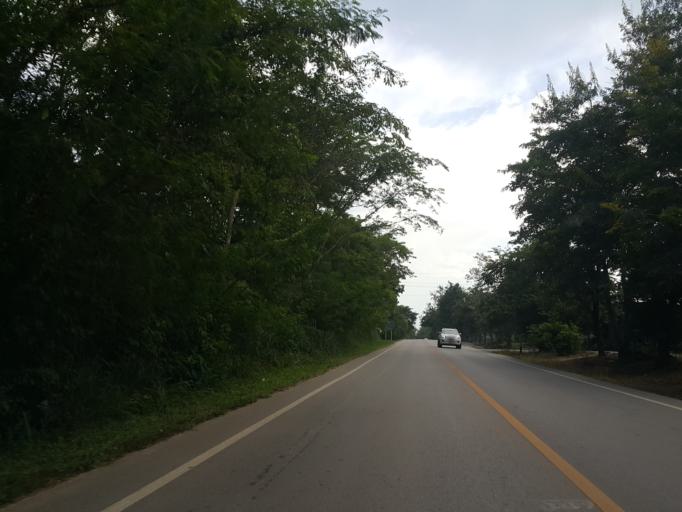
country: TH
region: Chiang Mai
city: Phrao
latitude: 19.3223
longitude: 99.1900
